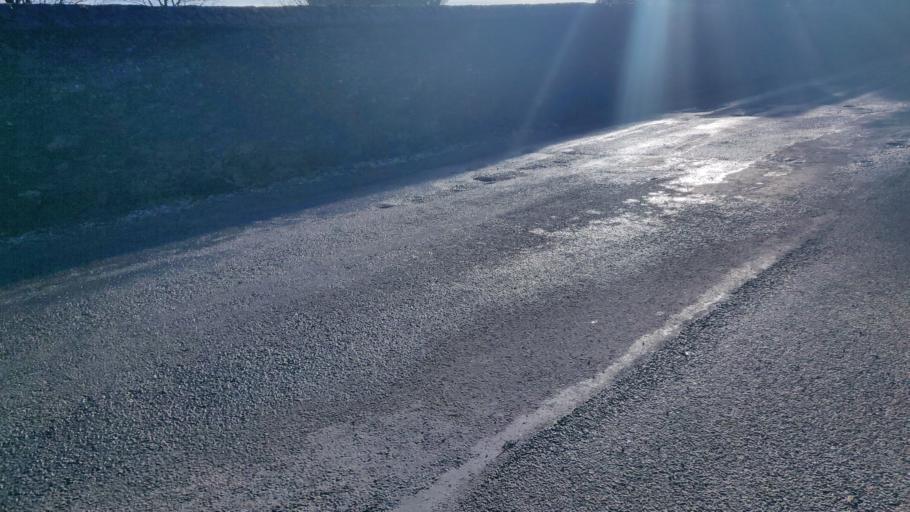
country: IE
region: Munster
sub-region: County Cork
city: Passage West
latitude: 51.8504
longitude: -8.3439
